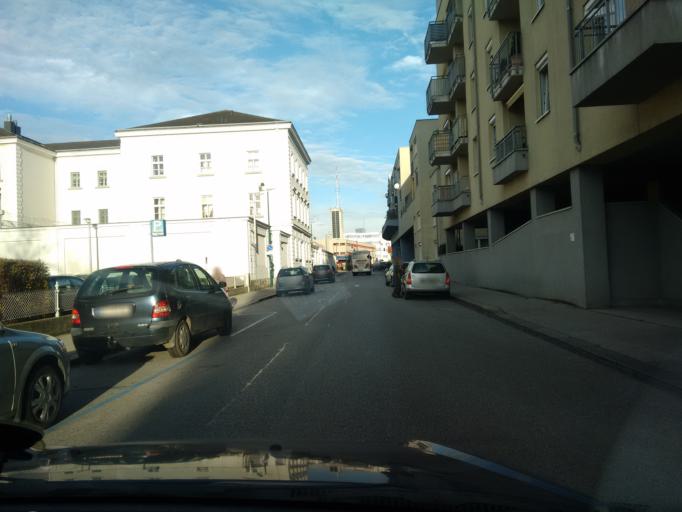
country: AT
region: Upper Austria
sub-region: Wels-Land
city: Thalheim bei Wels
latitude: 48.1570
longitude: 14.0202
